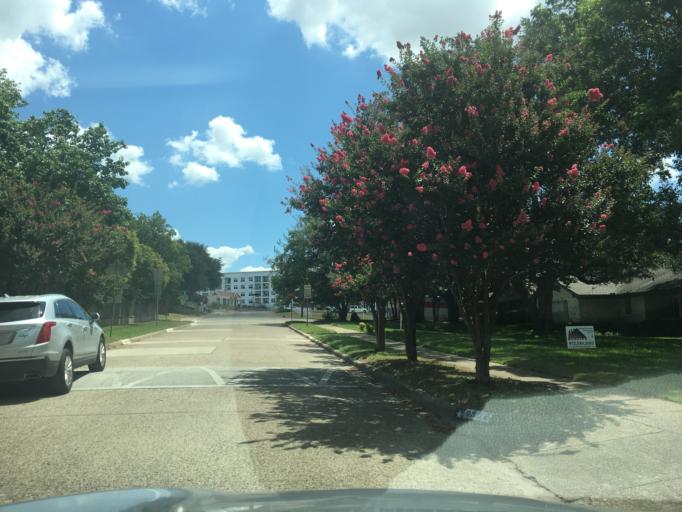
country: US
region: Texas
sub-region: Dallas County
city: Highland Park
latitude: 32.8653
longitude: -96.7150
